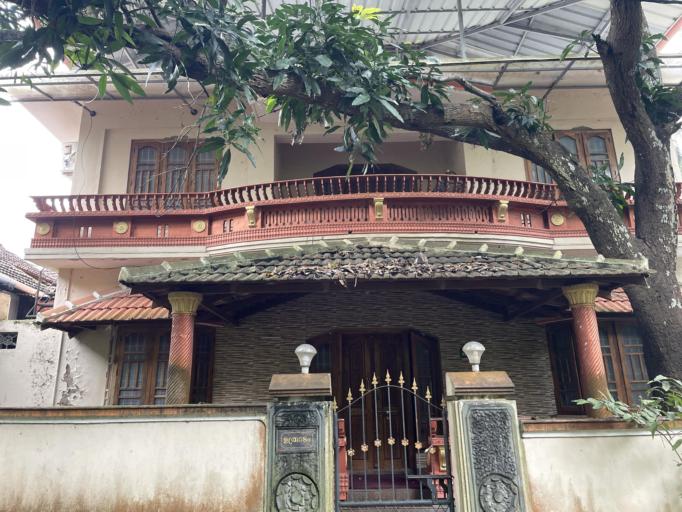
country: IN
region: Kerala
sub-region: Palakkad district
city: Chittur
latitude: 10.6918
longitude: 76.7416
